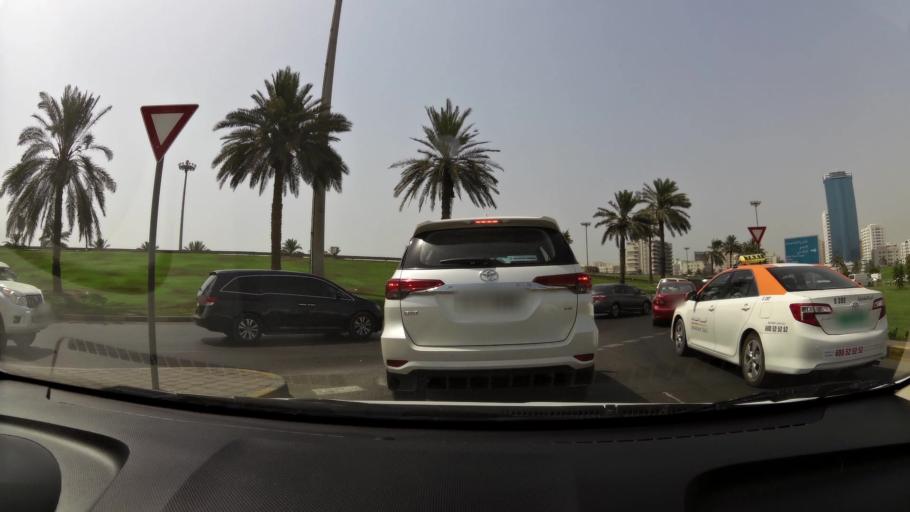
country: AE
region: Ash Shariqah
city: Sharjah
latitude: 25.3485
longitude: 55.3828
